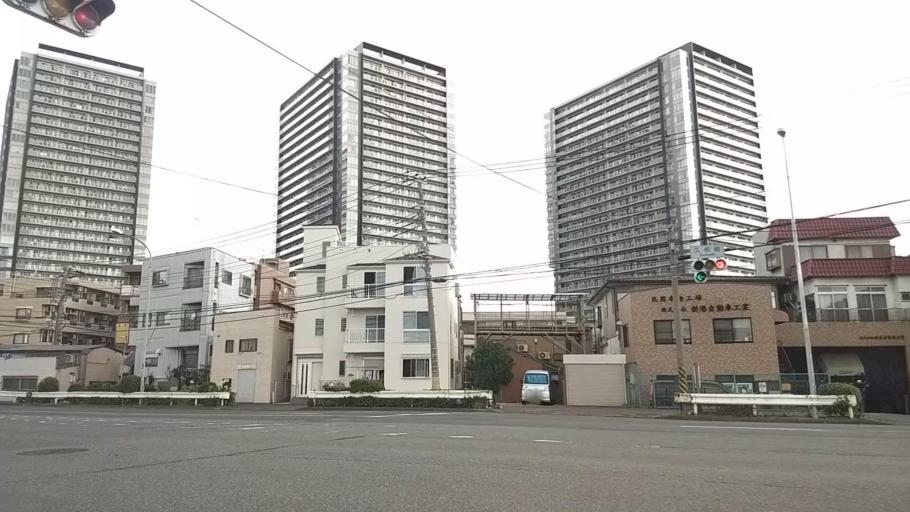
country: JP
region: Kanagawa
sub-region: Kawasaki-shi
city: Kawasaki
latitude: 35.5340
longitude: 139.7144
